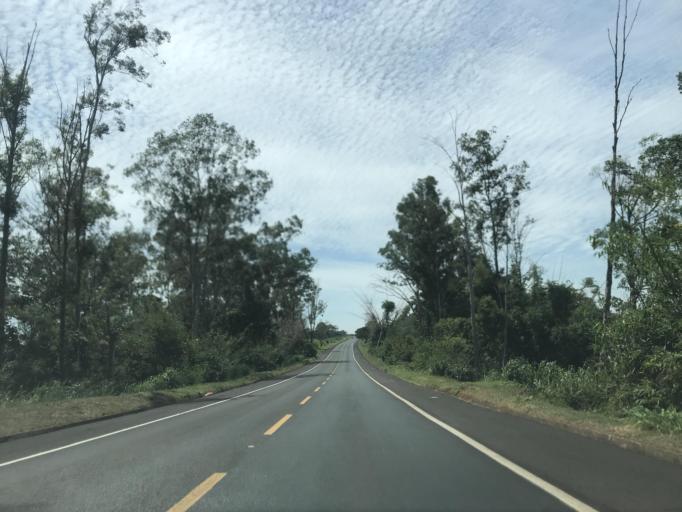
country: BR
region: Parana
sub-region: Paranavai
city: Paranavai
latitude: -22.9989
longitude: -52.5702
